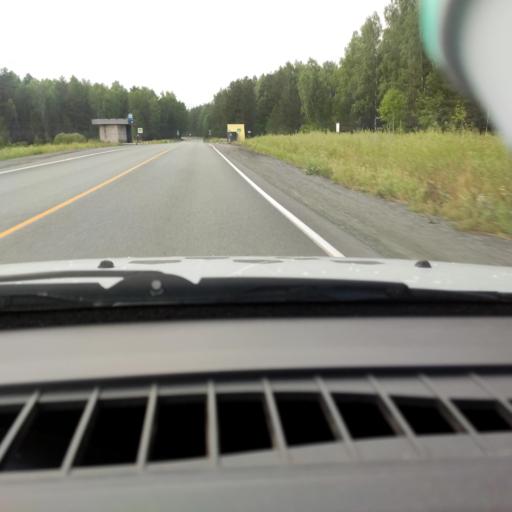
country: RU
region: Chelyabinsk
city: Turgoyak
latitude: 55.2663
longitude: 60.1975
